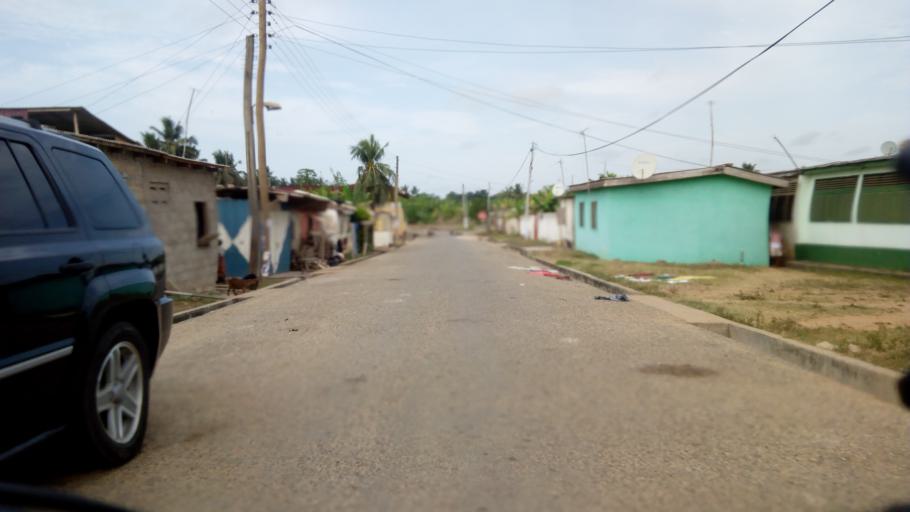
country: GH
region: Central
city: Cape Coast
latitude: 5.1028
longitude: -1.2784
